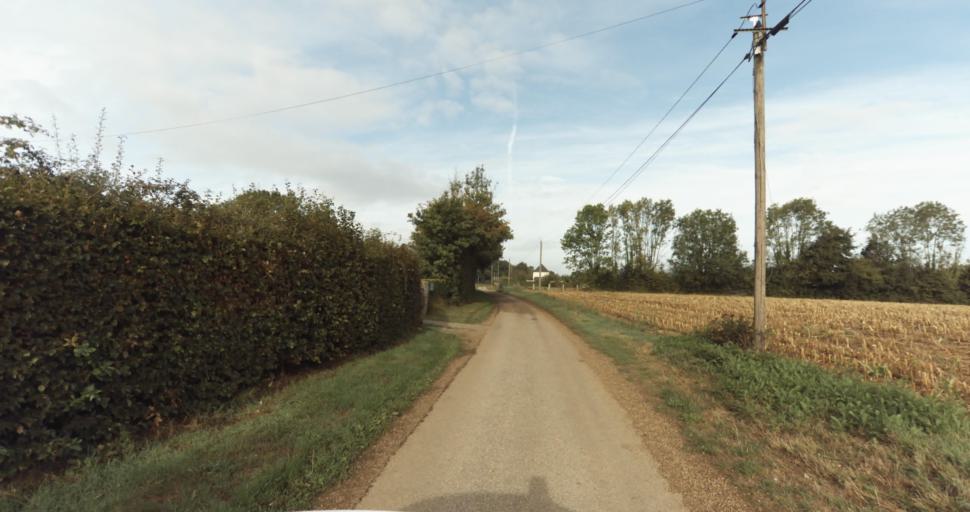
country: FR
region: Lower Normandy
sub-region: Departement de l'Orne
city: Vimoutiers
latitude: 48.9013
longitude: 0.2907
